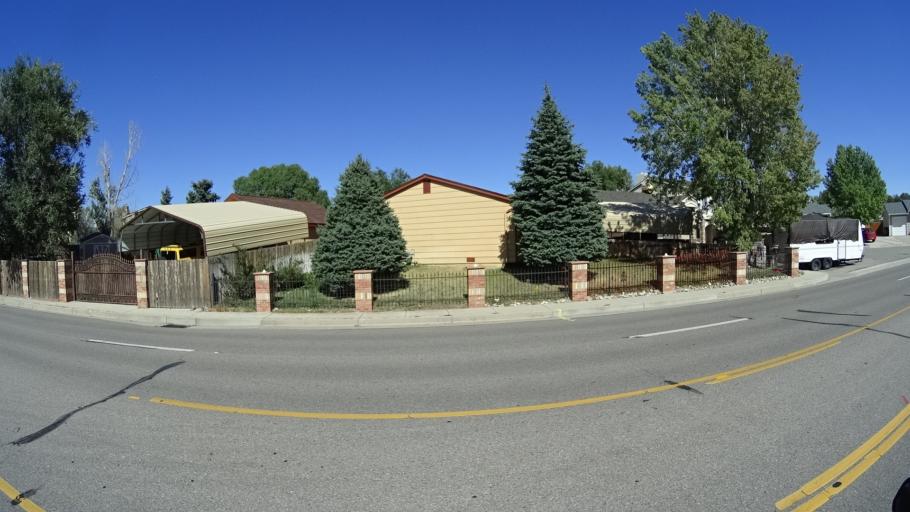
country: US
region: Colorado
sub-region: El Paso County
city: Stratmoor
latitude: 38.7913
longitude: -104.7397
